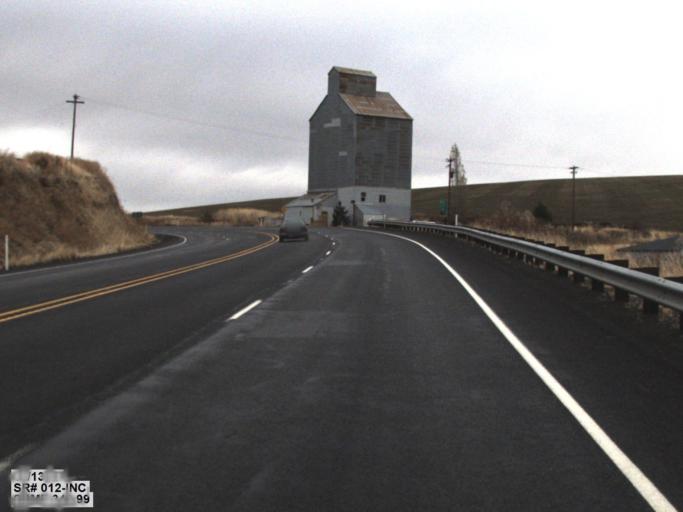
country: US
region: Washington
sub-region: Walla Walla County
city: Waitsburg
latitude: 46.1646
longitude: -118.1308
